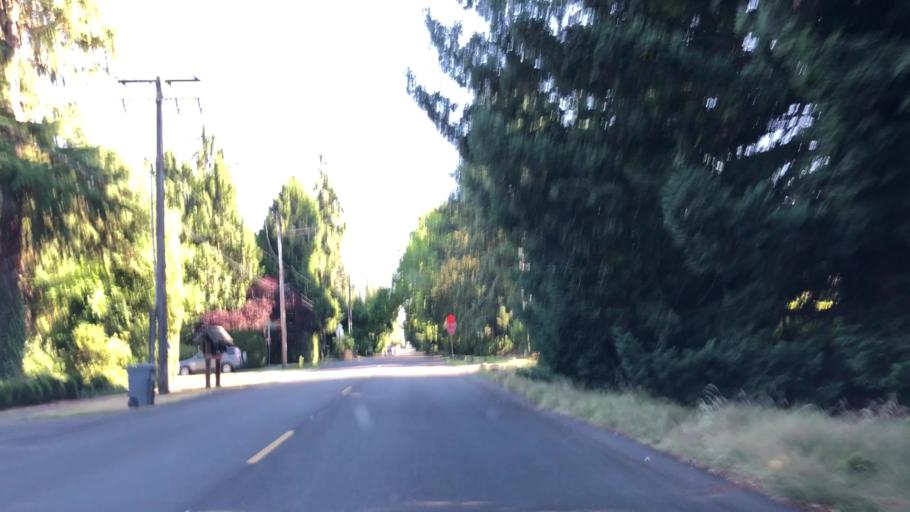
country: US
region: Washington
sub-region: King County
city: Medina
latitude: 47.6327
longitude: -122.2386
